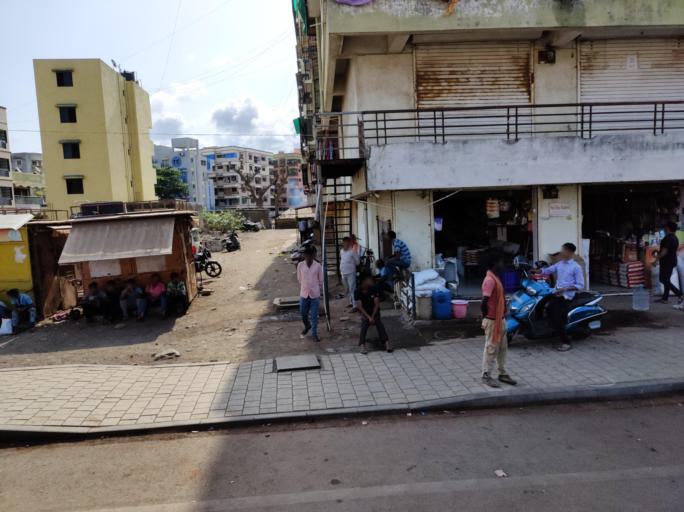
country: IN
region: Daman and Diu
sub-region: Daman District
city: Daman
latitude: 20.4183
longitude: 72.8374
